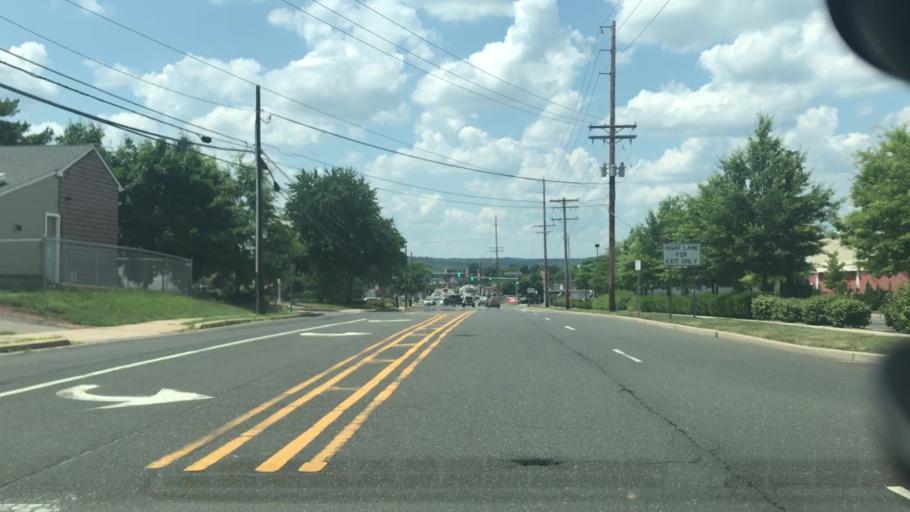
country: US
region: New Jersey
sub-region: Hunterdon County
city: Flemington
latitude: 40.4984
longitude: -74.8517
